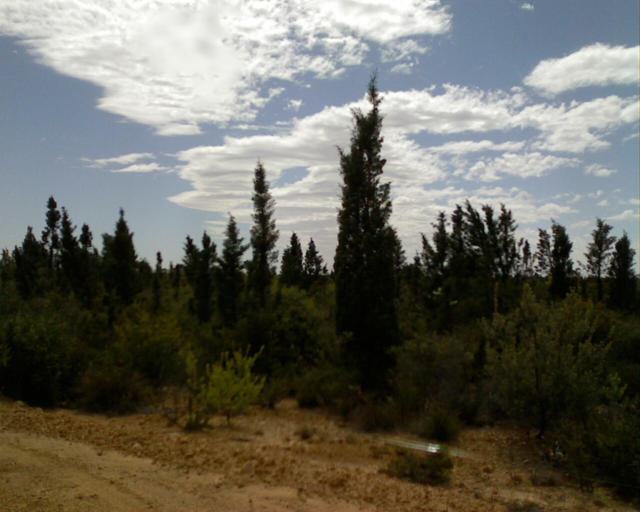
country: AU
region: Western Australia
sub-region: Moora
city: Moora
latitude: -30.0611
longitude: 115.6677
